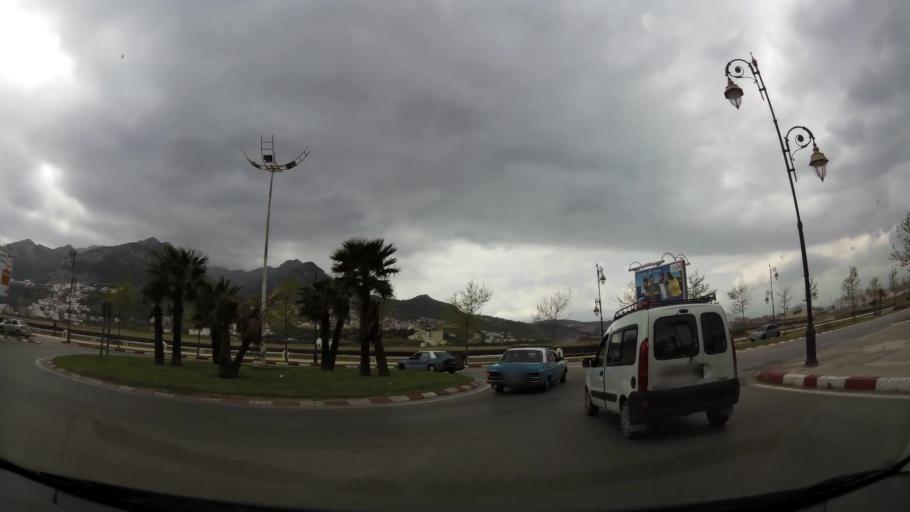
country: MA
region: Tanger-Tetouan
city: Tetouan
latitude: 35.5654
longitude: -5.3815
